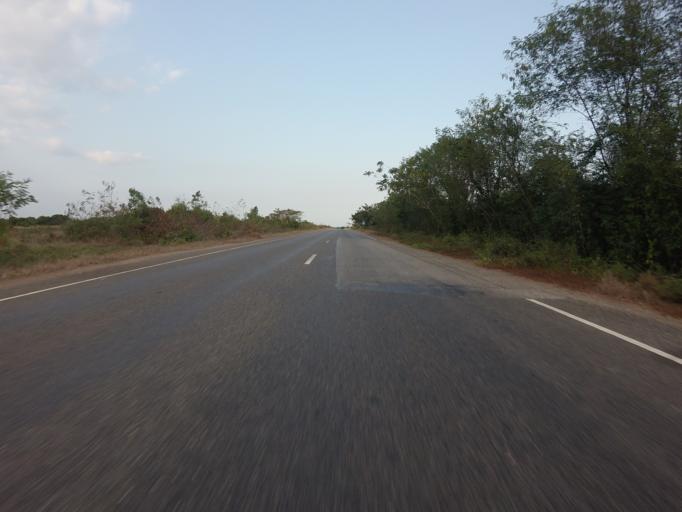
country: GH
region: Volta
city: Anloga
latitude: 6.0808
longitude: 0.5763
